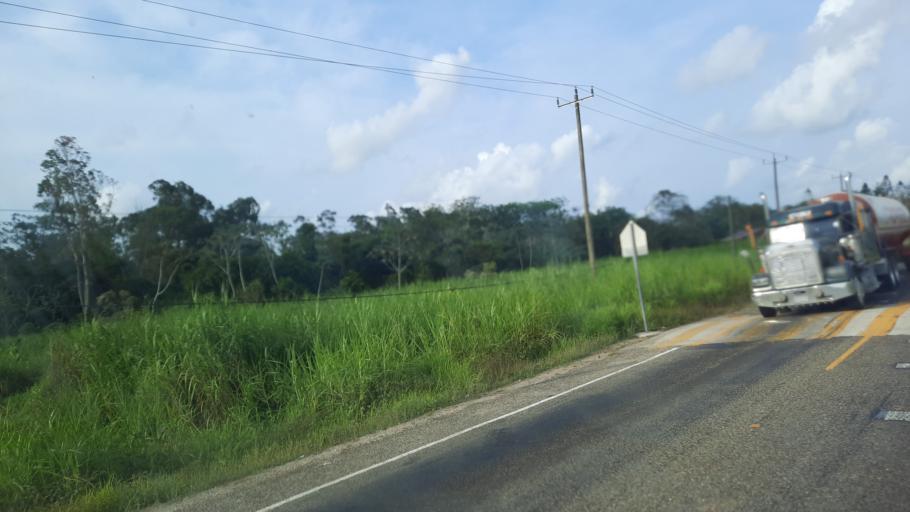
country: BZ
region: Stann Creek
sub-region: Dangriga
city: Dangriga
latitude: 17.0001
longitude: -88.3120
